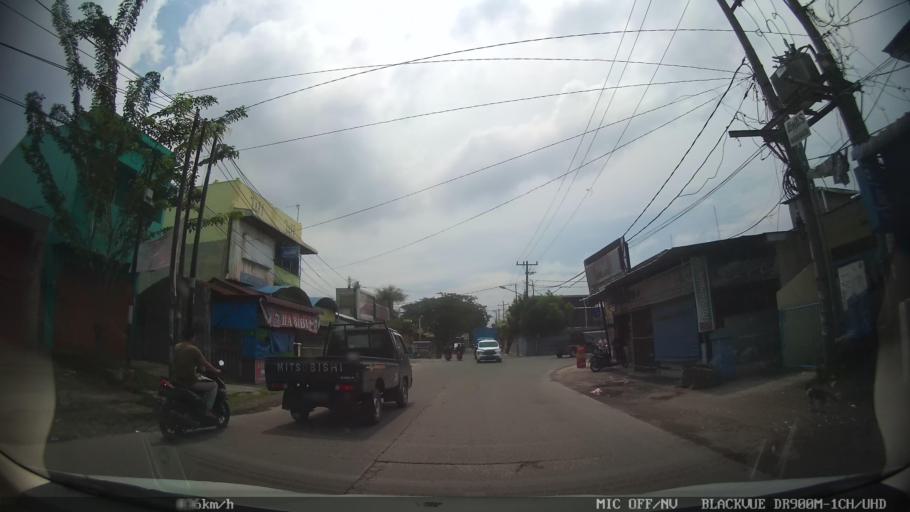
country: ID
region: North Sumatra
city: Medan
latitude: 3.6432
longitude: 98.6703
